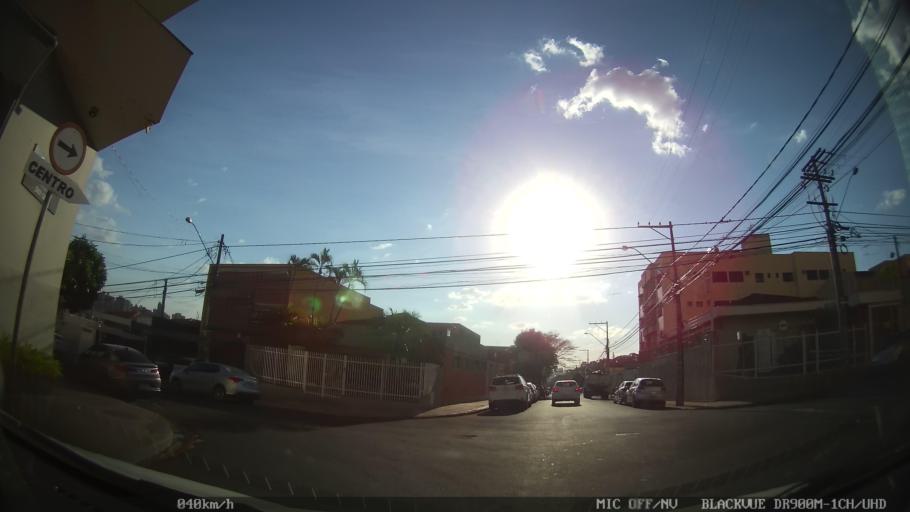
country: BR
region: Sao Paulo
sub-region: Ribeirao Preto
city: Ribeirao Preto
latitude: -21.1788
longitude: -47.7967
